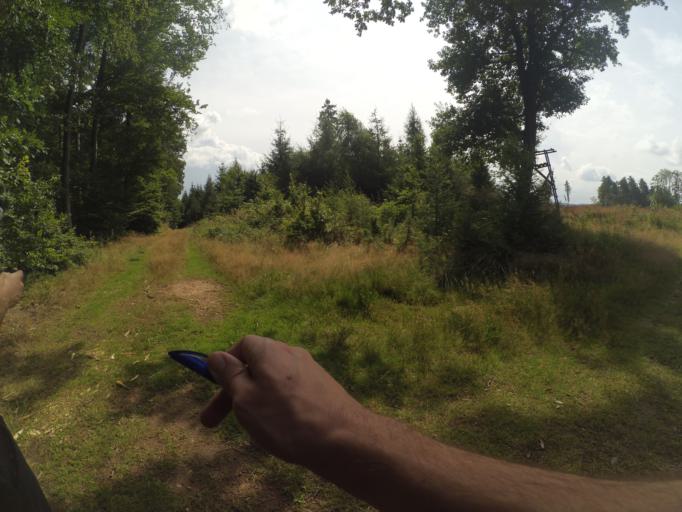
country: DE
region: Hesse
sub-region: Regierungsbezirk Kassel
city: Kirchheim
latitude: 50.8632
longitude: 9.5324
